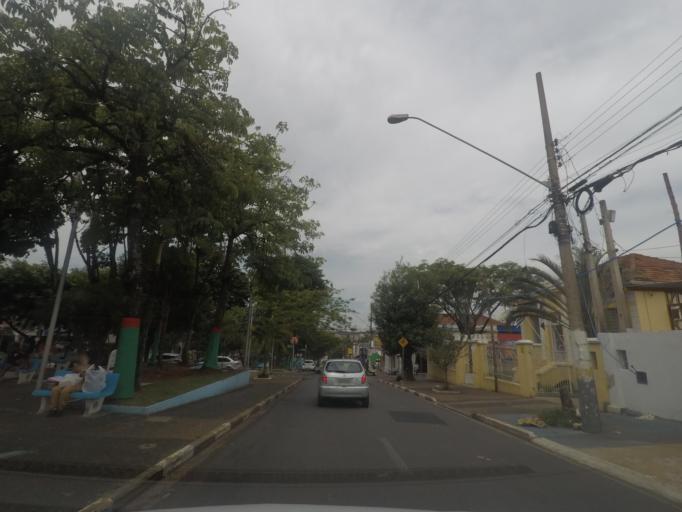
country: BR
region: Sao Paulo
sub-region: Sumare
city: Sumare
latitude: -22.8220
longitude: -47.2666
